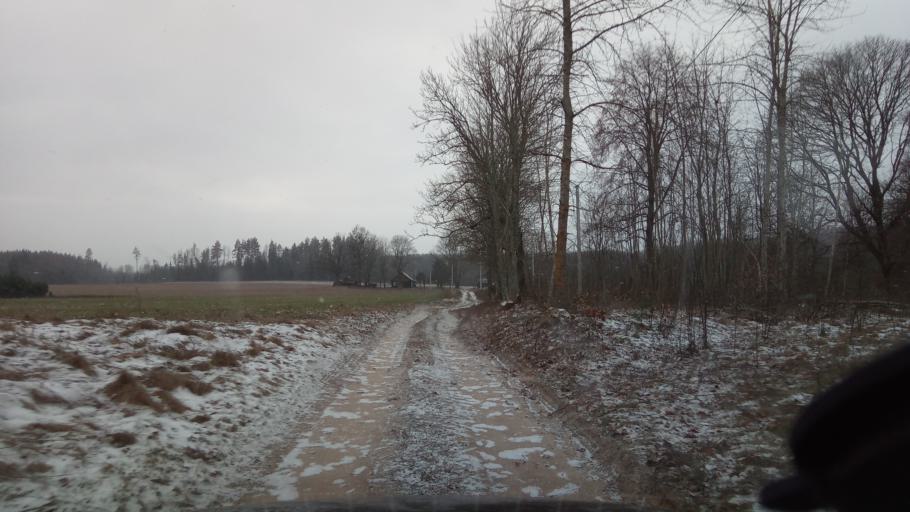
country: LT
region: Alytaus apskritis
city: Varena
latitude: 54.1308
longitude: 24.6819
